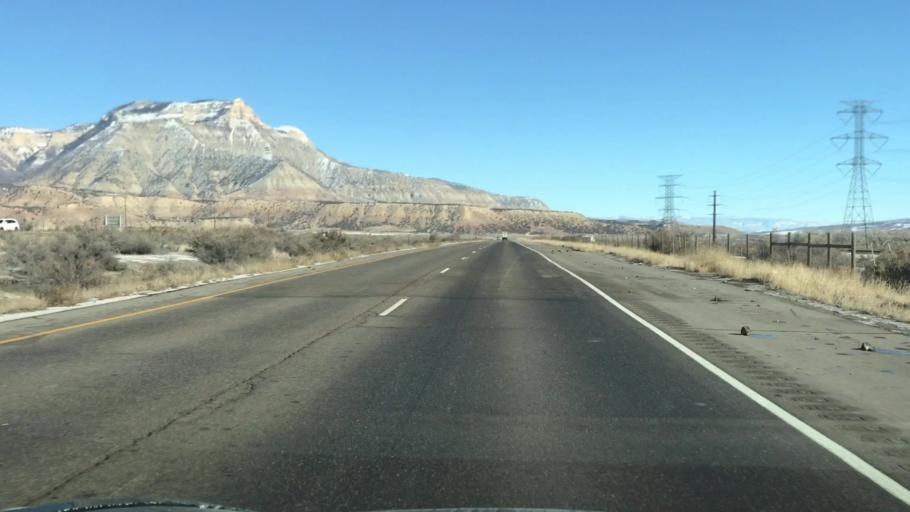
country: US
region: Colorado
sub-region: Garfield County
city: Parachute
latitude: 39.4681
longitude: -108.0314
